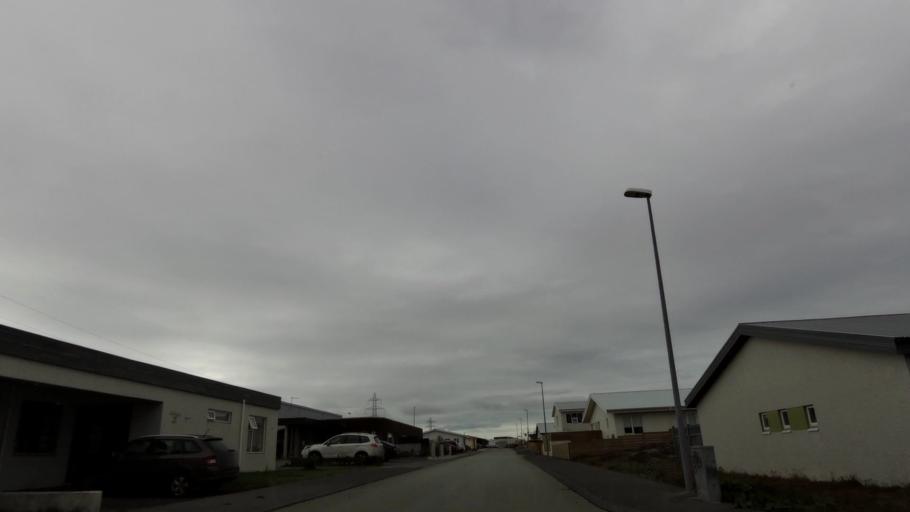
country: IS
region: Capital Region
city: Hafnarfjoerdur
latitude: 64.0431
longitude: -21.9619
